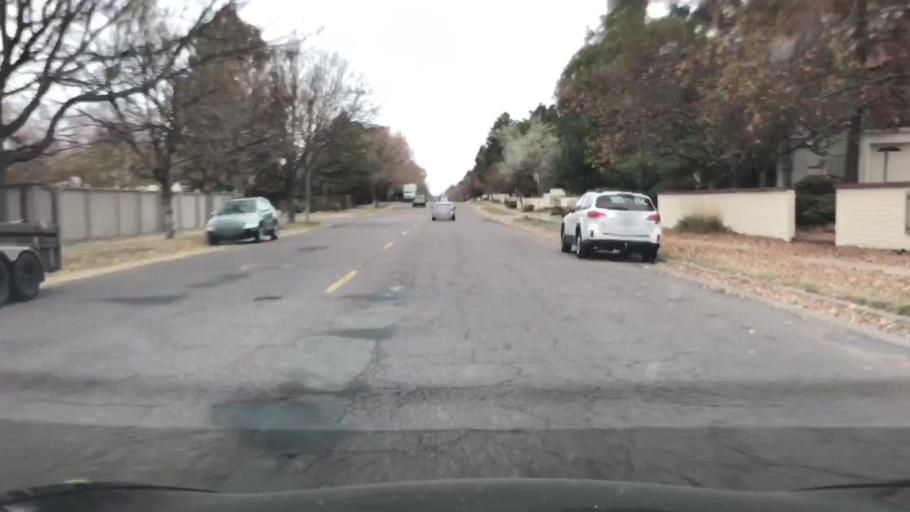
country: US
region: Colorado
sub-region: Arapahoe County
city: Glendale
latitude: 39.6868
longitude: -104.8944
